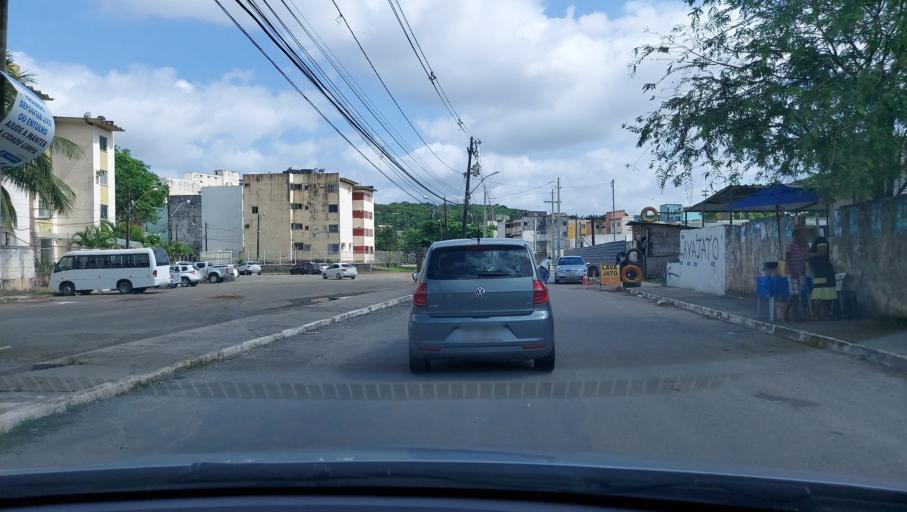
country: BR
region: Bahia
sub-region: Salvador
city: Salvador
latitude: -12.9644
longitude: -38.4301
